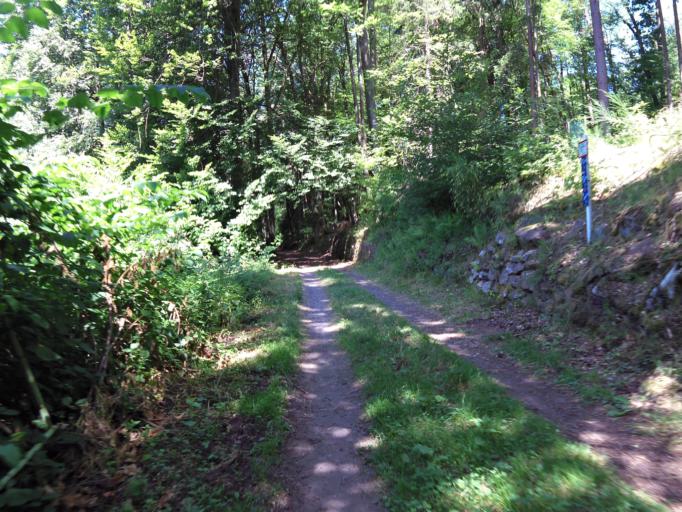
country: DE
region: Rheinland-Pfalz
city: Frankeneck
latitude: 49.3654
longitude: 8.0368
